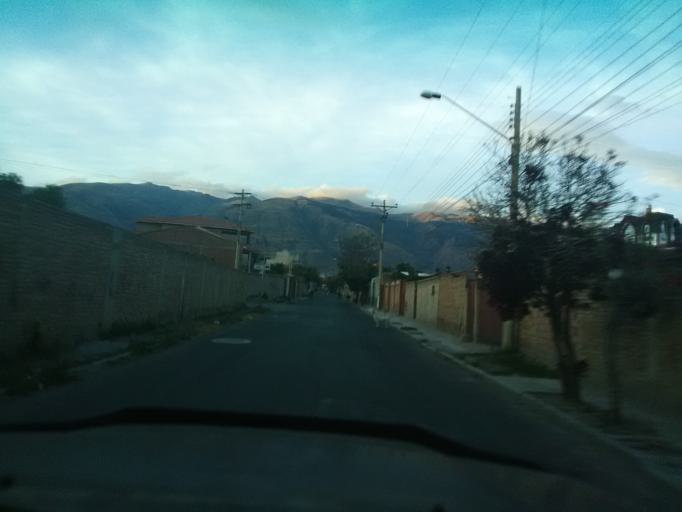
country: BO
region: Cochabamba
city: Cochabamba
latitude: -17.3721
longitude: -66.1904
